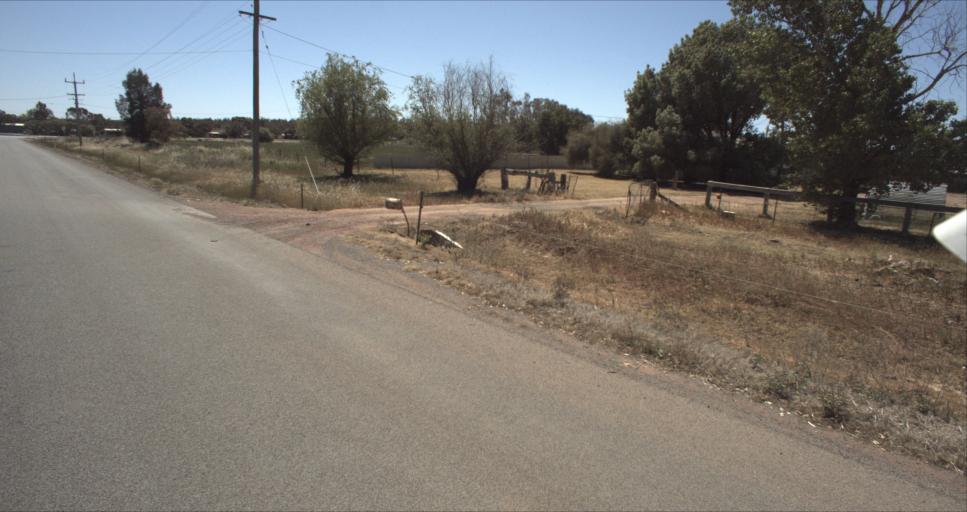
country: AU
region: New South Wales
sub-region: Leeton
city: Leeton
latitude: -34.4293
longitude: 146.2999
